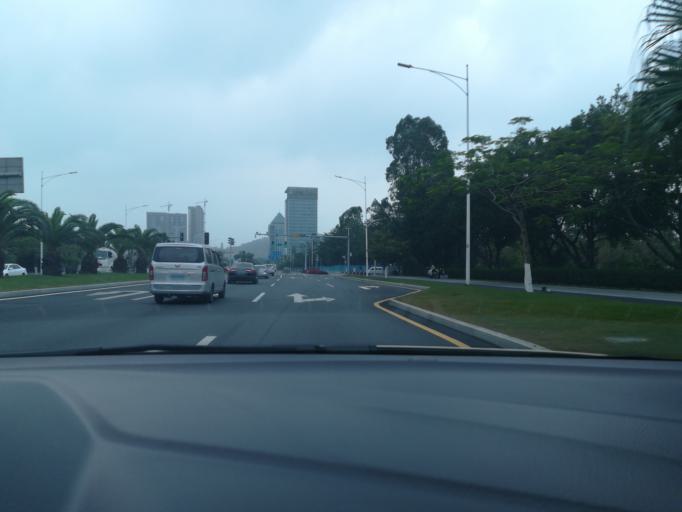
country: CN
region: Guangdong
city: Nansha
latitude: 22.7779
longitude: 113.5964
